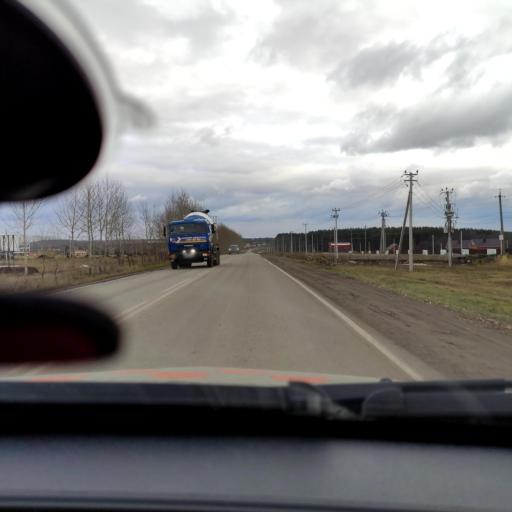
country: RU
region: Bashkortostan
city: Kabakovo
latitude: 54.6144
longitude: 56.1497
